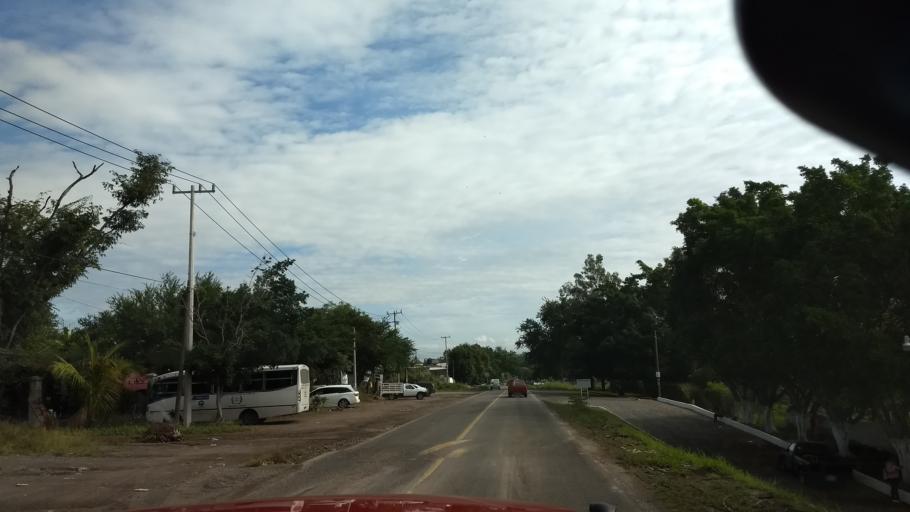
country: MX
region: Jalisco
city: Tuxpan
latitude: 19.5485
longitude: -103.3956
